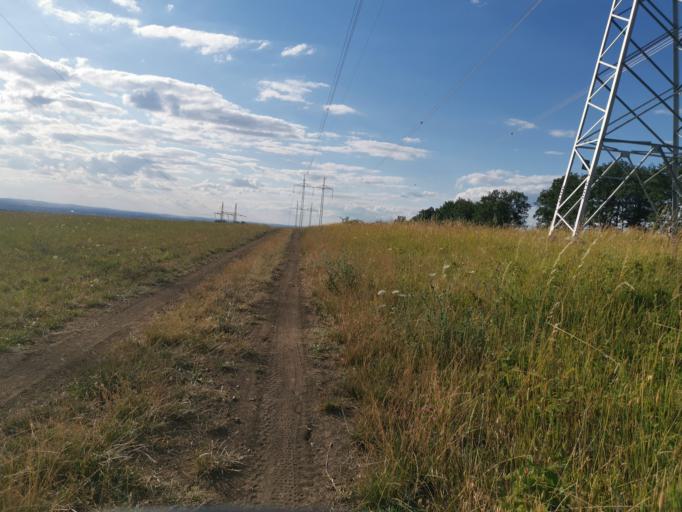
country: CZ
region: South Moravian
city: Sudomerice
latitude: 48.8113
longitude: 17.2879
